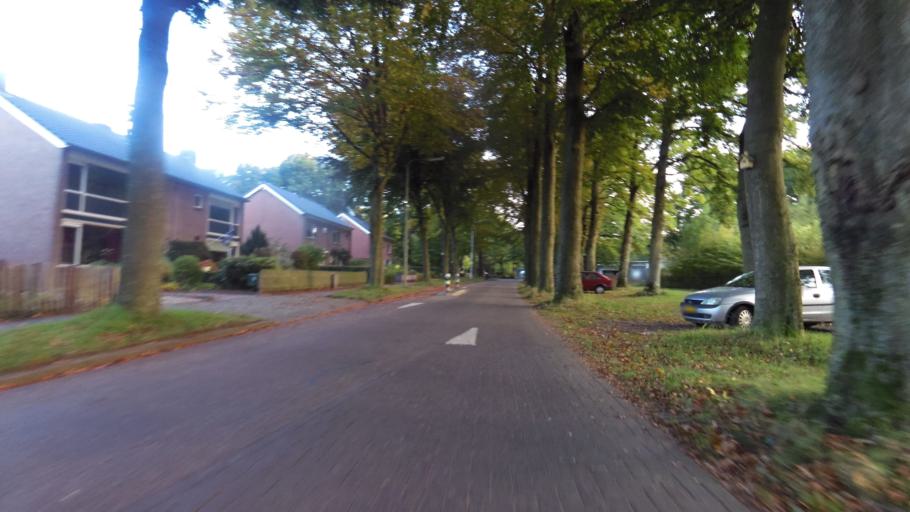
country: NL
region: Gelderland
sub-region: Gemeente Nunspeet
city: Nunspeet
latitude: 52.3317
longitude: 5.8258
